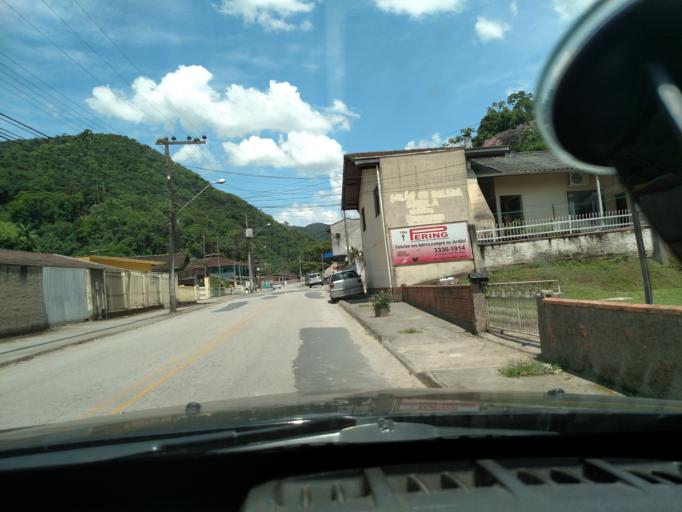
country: BR
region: Santa Catarina
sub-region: Blumenau
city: Blumenau
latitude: -26.9897
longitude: -49.0739
